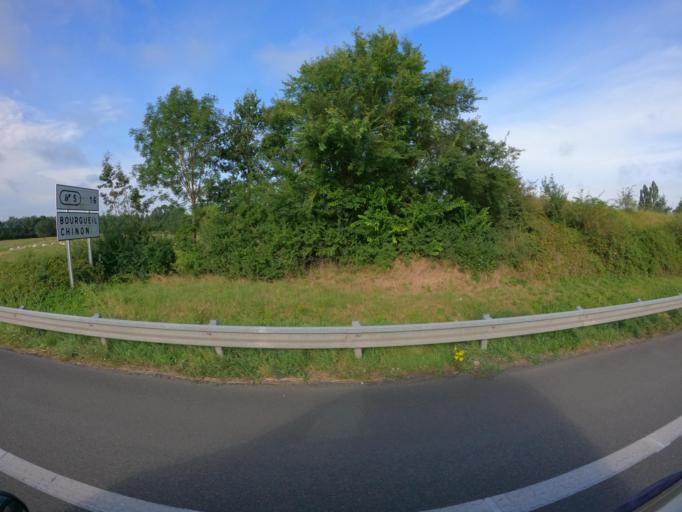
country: FR
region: Pays de la Loire
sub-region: Departement de Maine-et-Loire
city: Vivy
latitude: 47.3034
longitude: -0.0329
